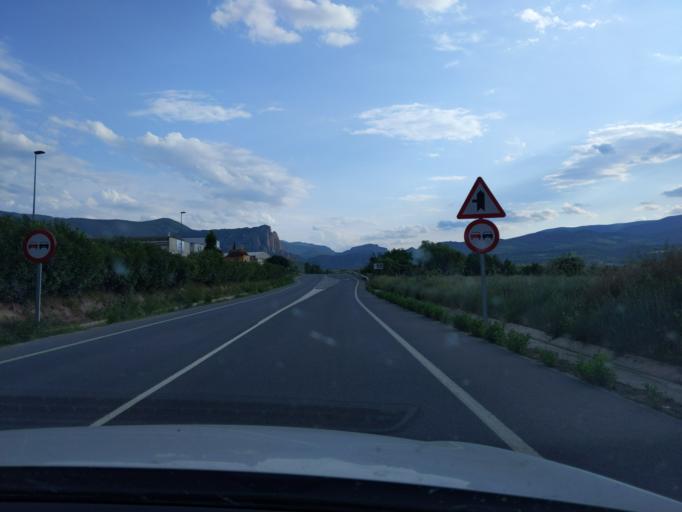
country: ES
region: La Rioja
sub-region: Provincia de La Rioja
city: Albelda de Iregua
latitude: 42.3471
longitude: -2.4796
